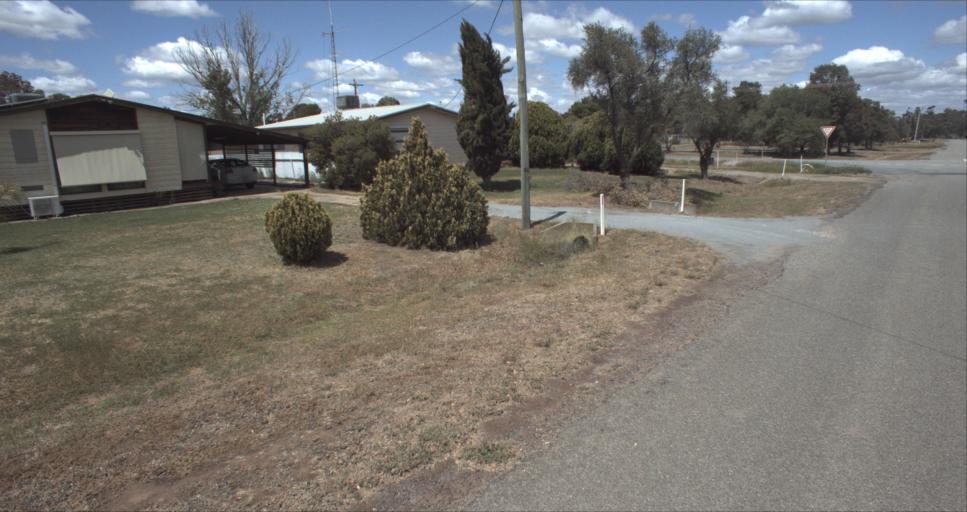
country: AU
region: New South Wales
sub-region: Murrumbidgee Shire
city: Darlington Point
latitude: -34.5194
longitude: 146.1833
